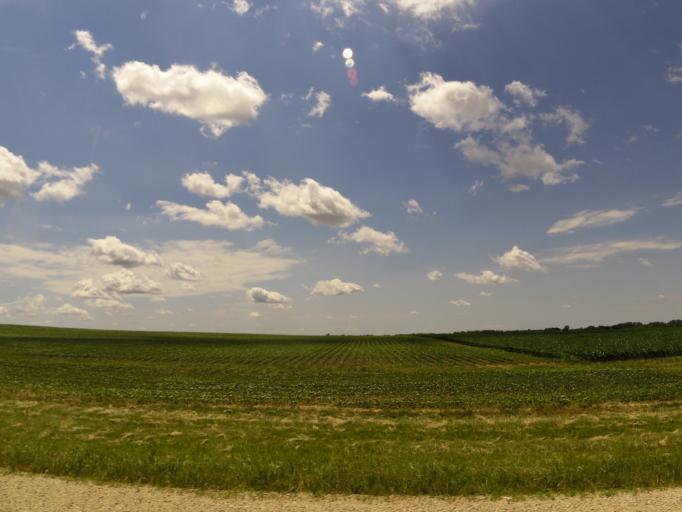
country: US
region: Iowa
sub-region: Fayette County
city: Oelwein
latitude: 42.7148
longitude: -91.9377
